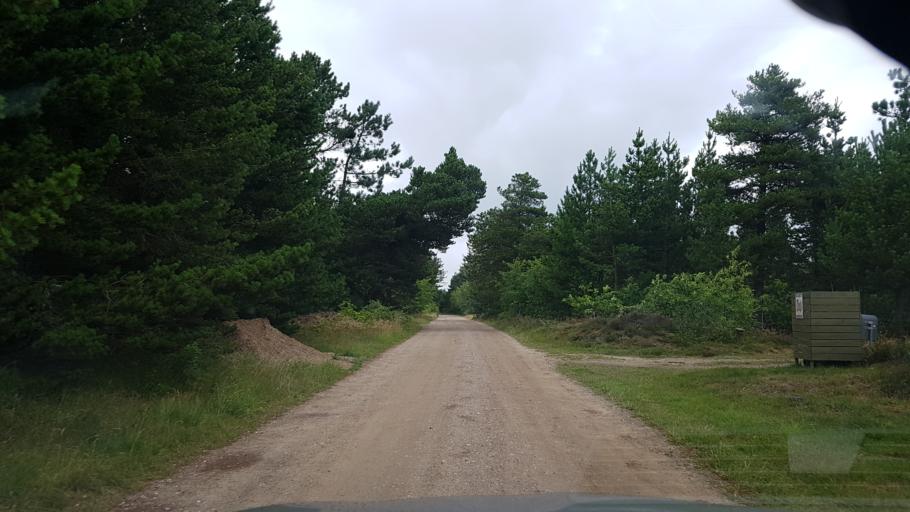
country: DE
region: Schleswig-Holstein
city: List
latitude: 55.1310
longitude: 8.5395
